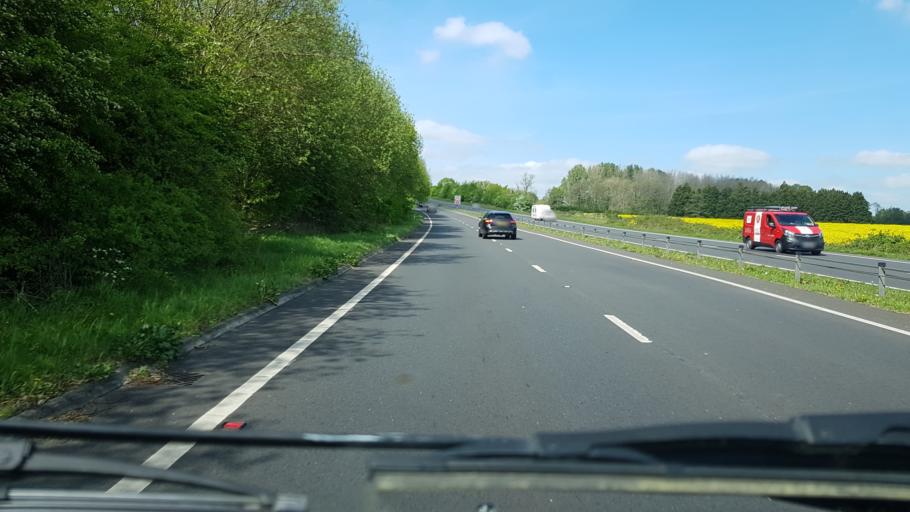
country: GB
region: England
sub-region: East Sussex
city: Wadhurst
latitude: 51.1045
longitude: 0.4044
